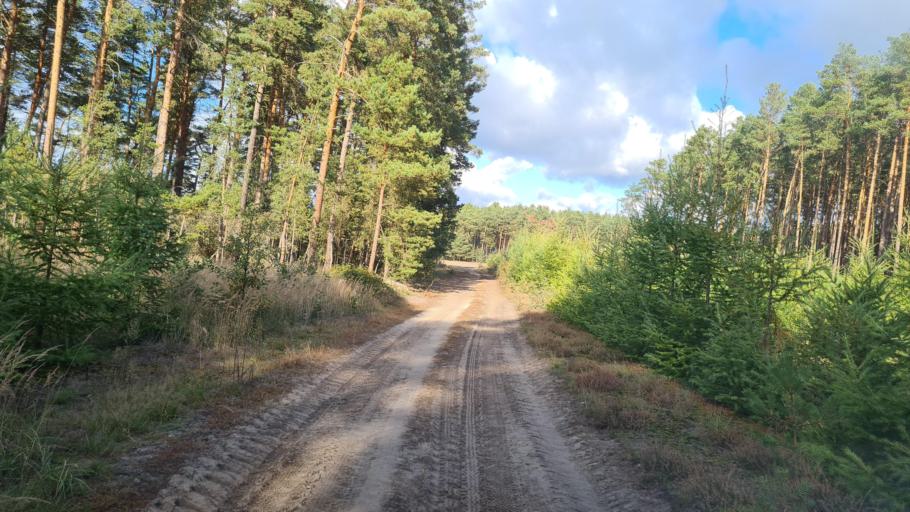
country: DE
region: Brandenburg
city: Vetschau
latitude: 51.7269
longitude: 14.0895
